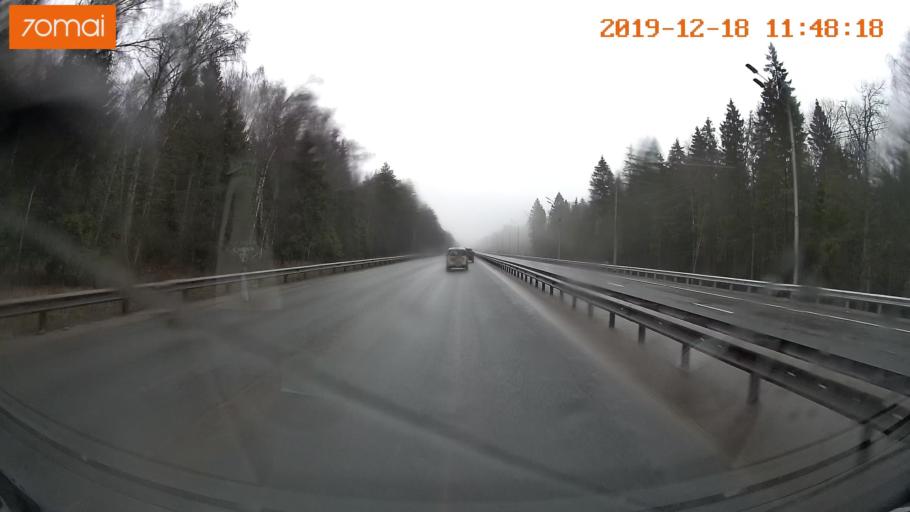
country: RU
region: Moskovskaya
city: Yershovo
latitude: 55.7666
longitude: 36.9022
